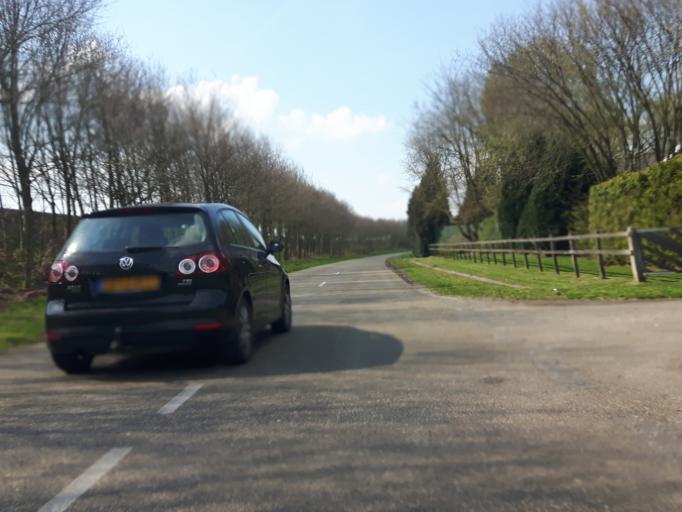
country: NL
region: Overijssel
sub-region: Gemeente Enschede
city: Enschede
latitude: 52.2059
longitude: 6.8302
